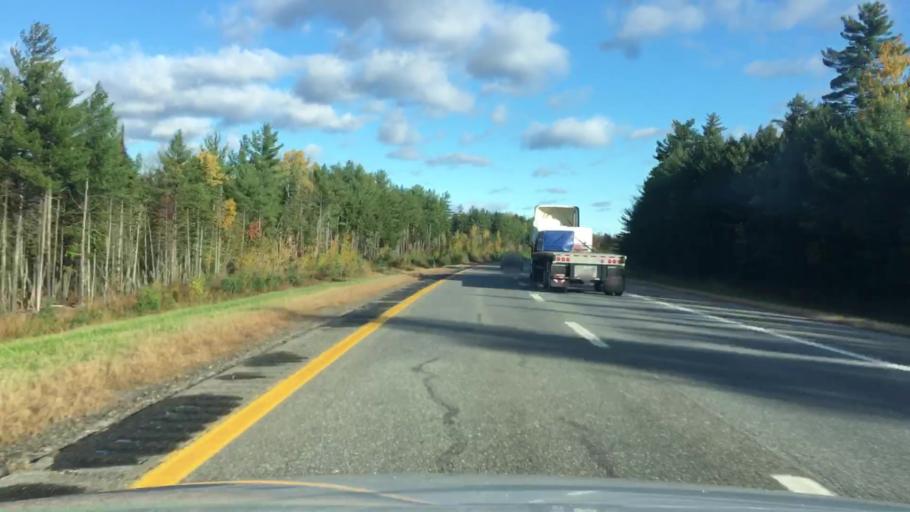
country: US
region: Maine
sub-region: Penobscot County
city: Greenbush
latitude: 45.1496
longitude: -68.7036
